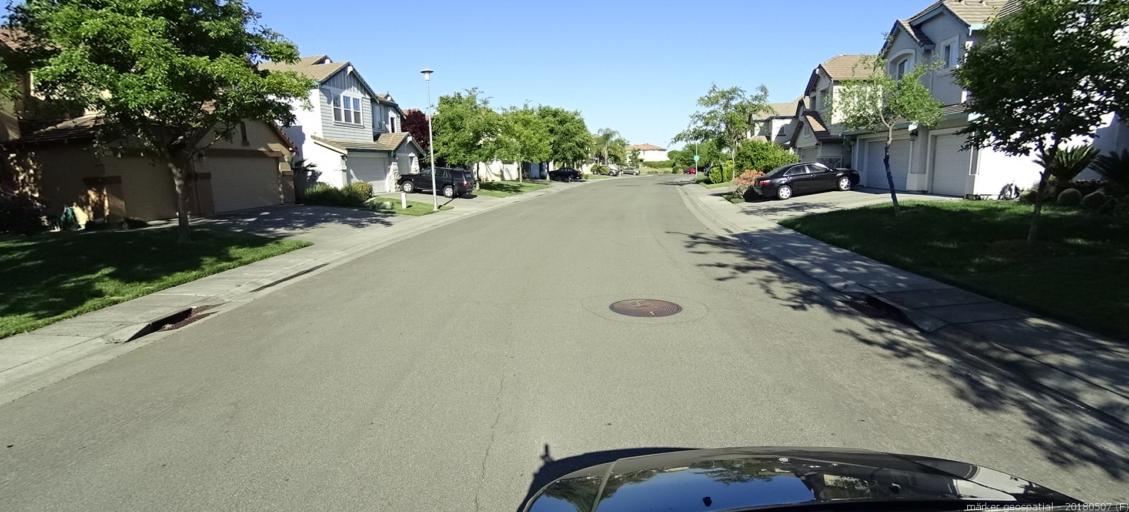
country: US
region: California
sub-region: Sacramento County
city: Rio Linda
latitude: 38.6648
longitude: -121.4974
